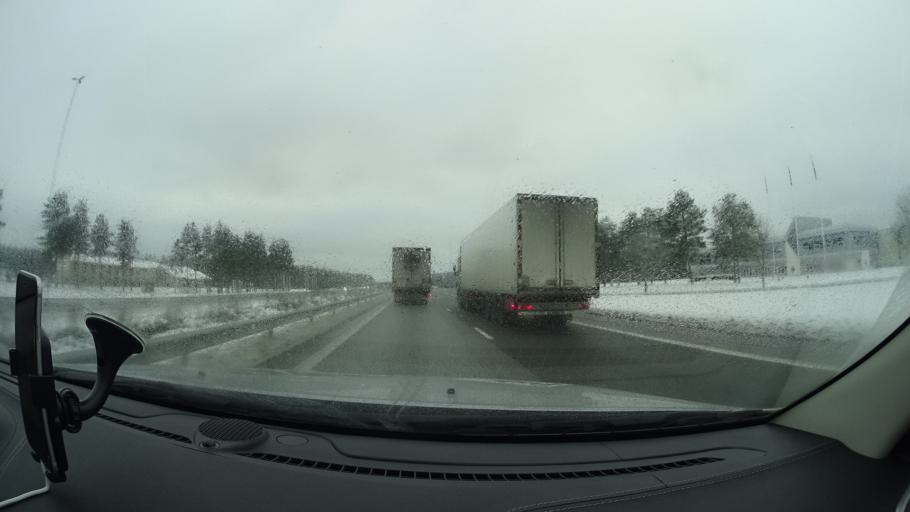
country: SE
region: Joenkoeping
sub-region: Vaggeryds Kommun
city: Skillingaryd
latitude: 57.4513
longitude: 14.0981
